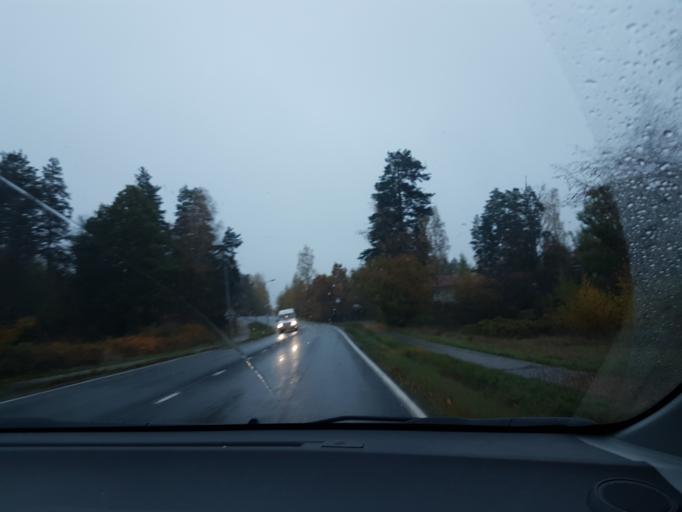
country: FI
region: Uusimaa
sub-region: Helsinki
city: Jaervenpaeae
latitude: 60.5345
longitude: 25.1115
